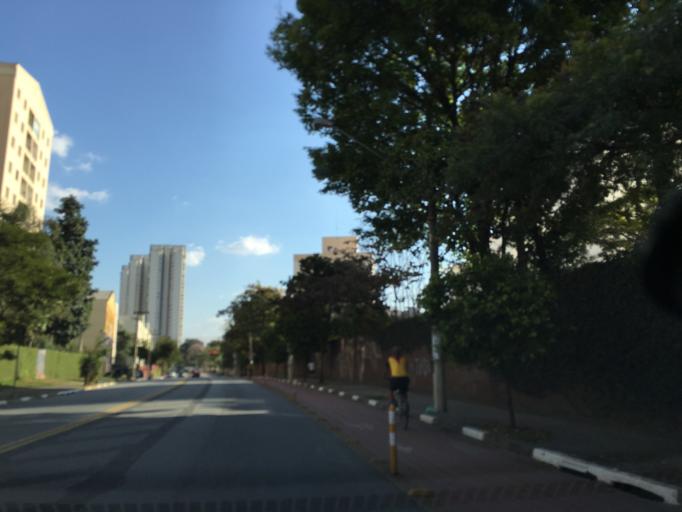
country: BR
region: Sao Paulo
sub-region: Sao Paulo
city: Sao Paulo
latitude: -23.4776
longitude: -46.6431
